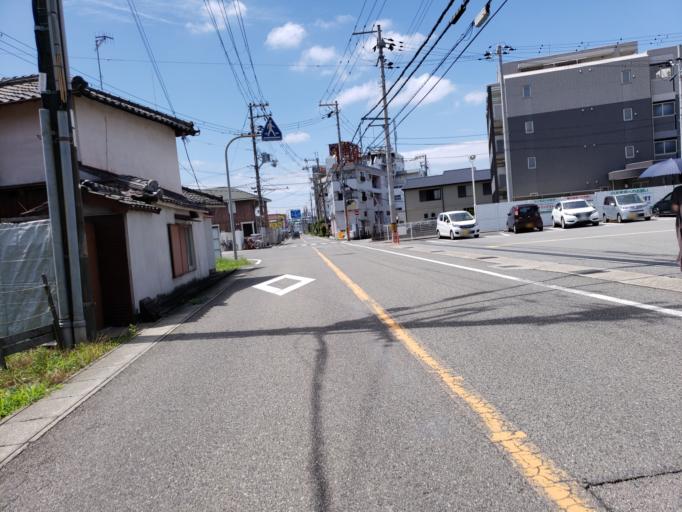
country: JP
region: Hyogo
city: Kakogawacho-honmachi
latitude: 34.7035
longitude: 134.8906
